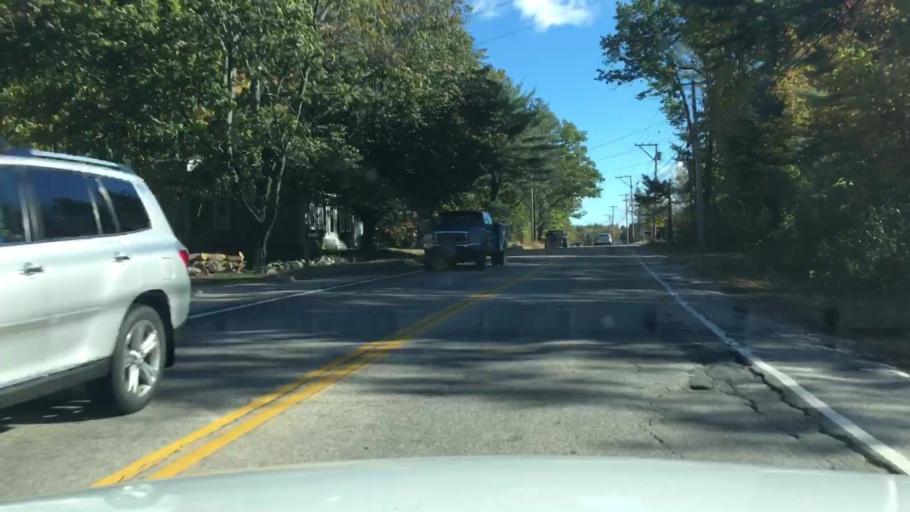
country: US
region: Maine
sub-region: York County
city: South Sanford
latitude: 43.4053
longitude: -70.7318
